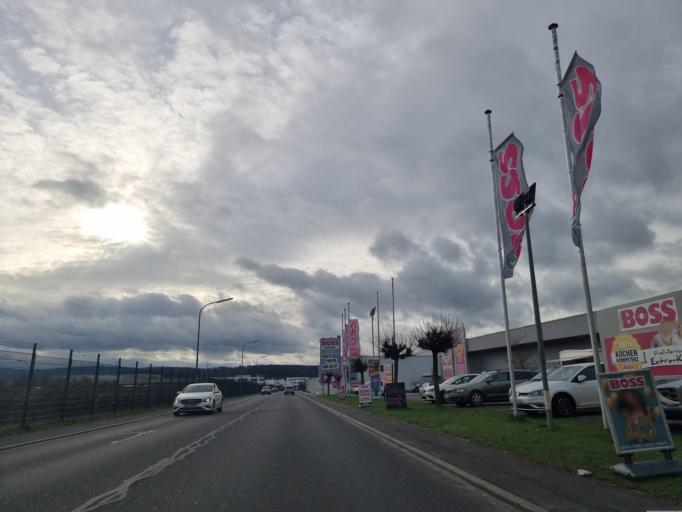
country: DE
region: Rheinland-Pfalz
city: Wittlich
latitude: 49.9872
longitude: 6.9088
